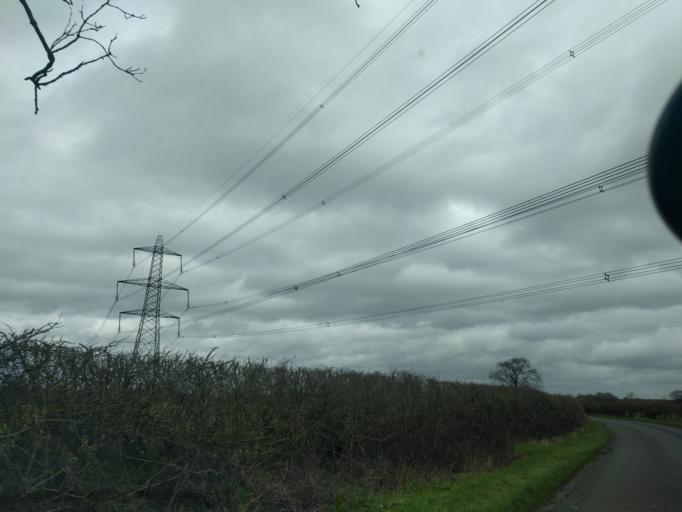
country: GB
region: England
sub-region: Wiltshire
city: Biddestone
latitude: 51.4764
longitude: -2.1964
